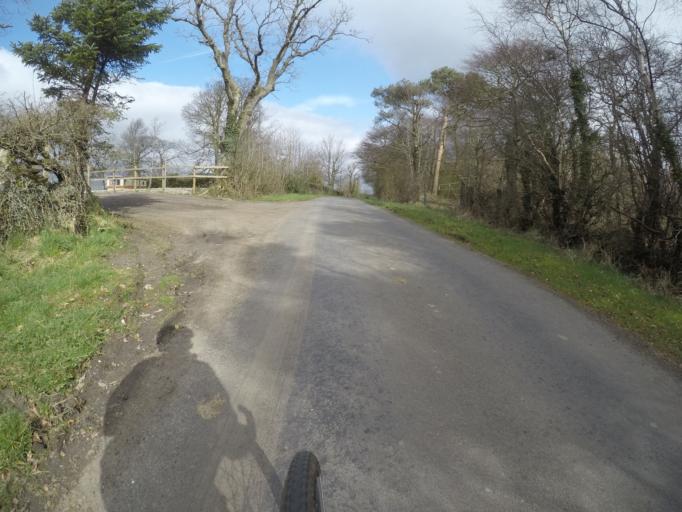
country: GB
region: Scotland
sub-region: North Ayrshire
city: Springside
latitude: 55.6521
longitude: -4.6136
